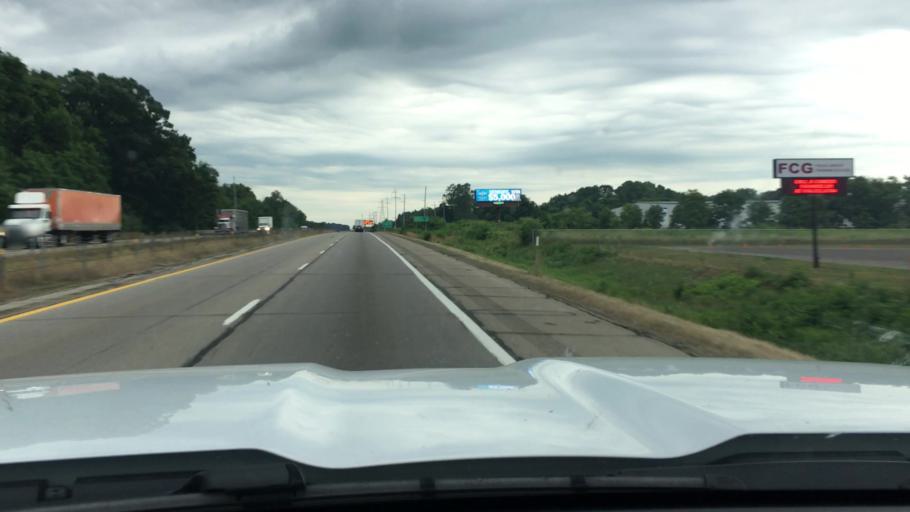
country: US
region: Michigan
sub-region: Kent County
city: Cutlerville
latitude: 42.8026
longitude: -85.6690
